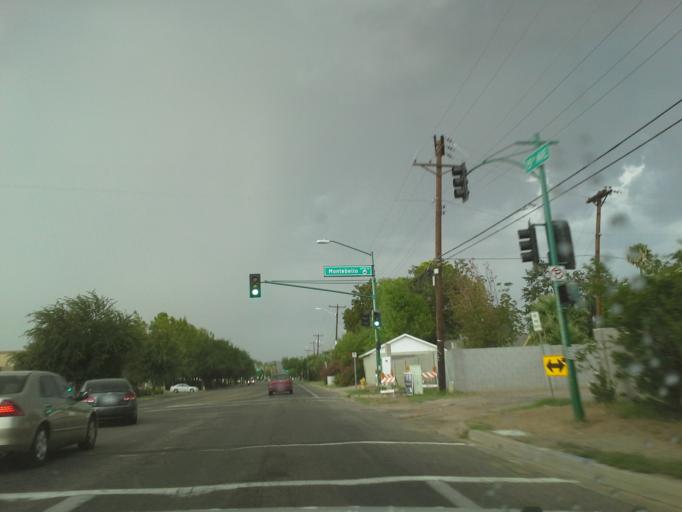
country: US
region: Arizona
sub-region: Maricopa County
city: Phoenix
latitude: 33.5201
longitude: -112.0911
